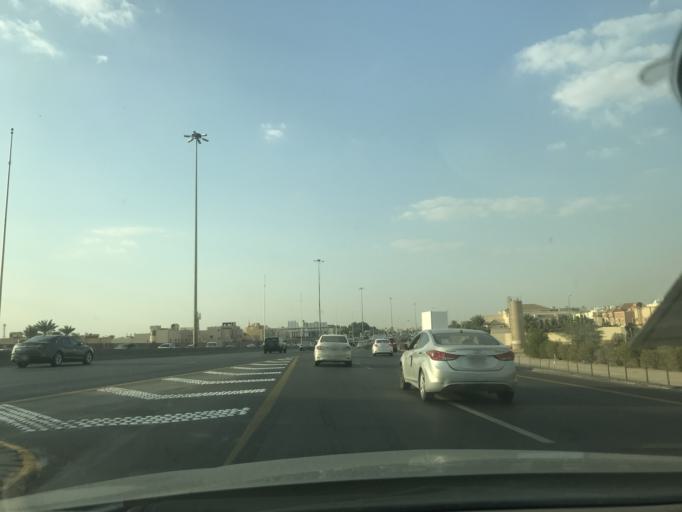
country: SA
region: Ar Riyad
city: Riyadh
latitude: 24.7401
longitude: 46.5883
